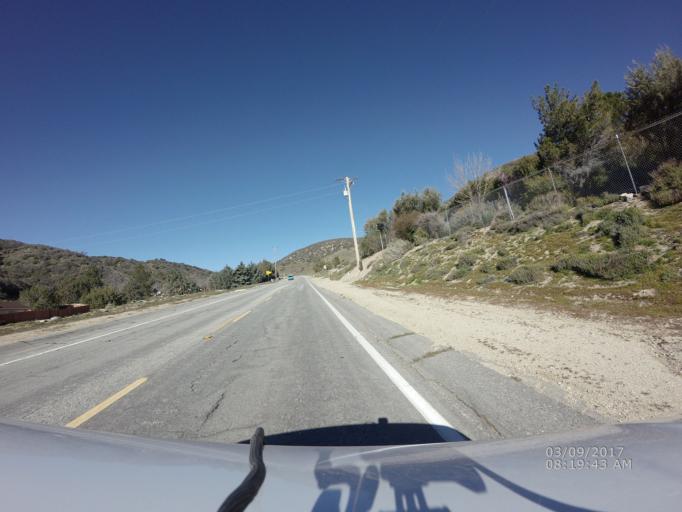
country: US
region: California
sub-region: Los Angeles County
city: Leona Valley
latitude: 34.6589
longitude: -118.3464
